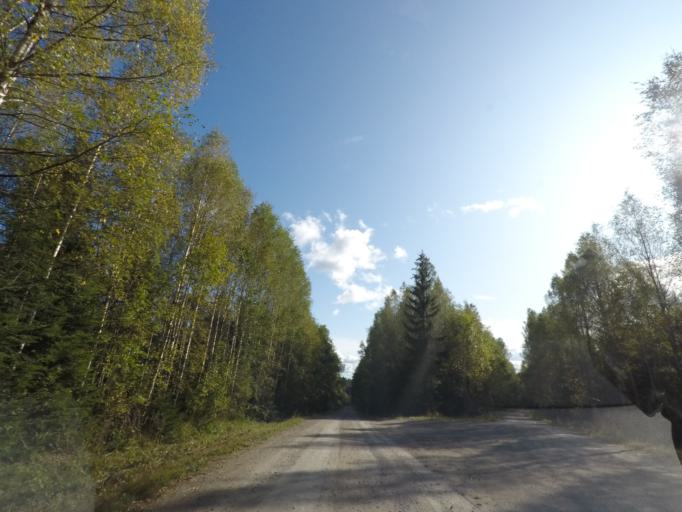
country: SE
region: Vaestmanland
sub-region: Skinnskattebergs Kommun
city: Skinnskatteberg
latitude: 59.8299
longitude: 15.5287
